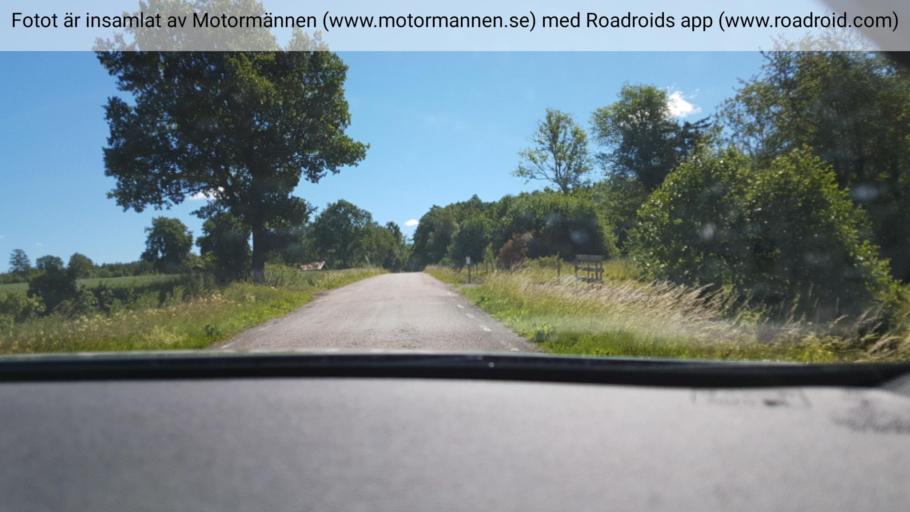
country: SE
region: Vaestra Goetaland
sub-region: Falkopings Kommun
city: Akarp
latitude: 58.1923
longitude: 13.7268
